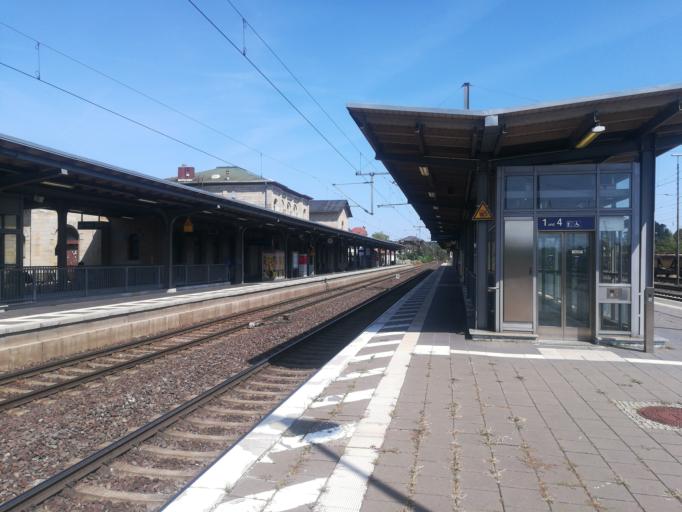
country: DE
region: Lower Saxony
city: Helmstedt
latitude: 52.2217
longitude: 11.0100
